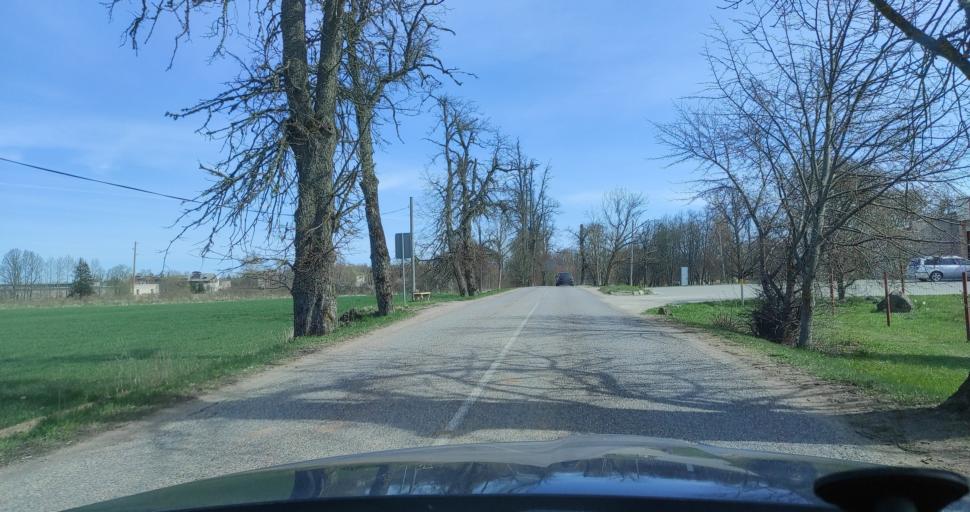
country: LV
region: Talsu Rajons
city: Talsi
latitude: 57.2229
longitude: 22.5122
